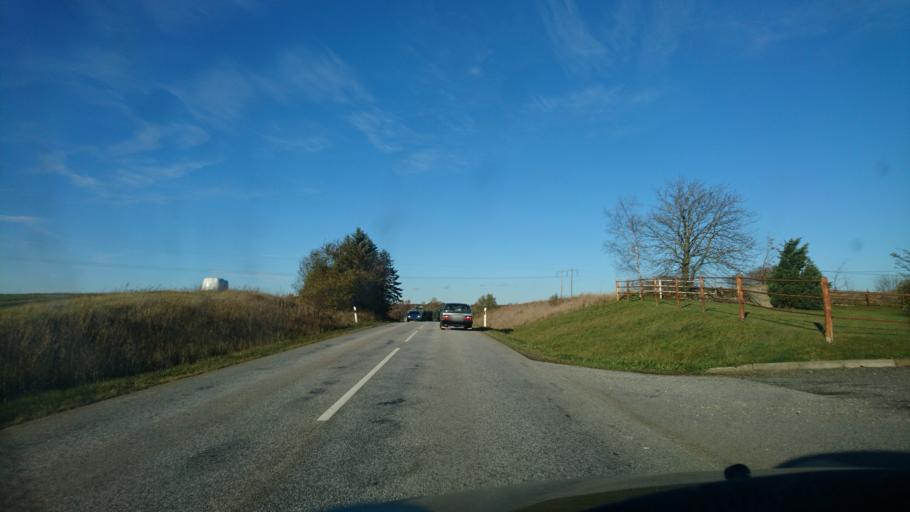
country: SE
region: Skane
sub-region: Tomelilla Kommun
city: Tomelilla
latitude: 55.5695
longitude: 13.9628
